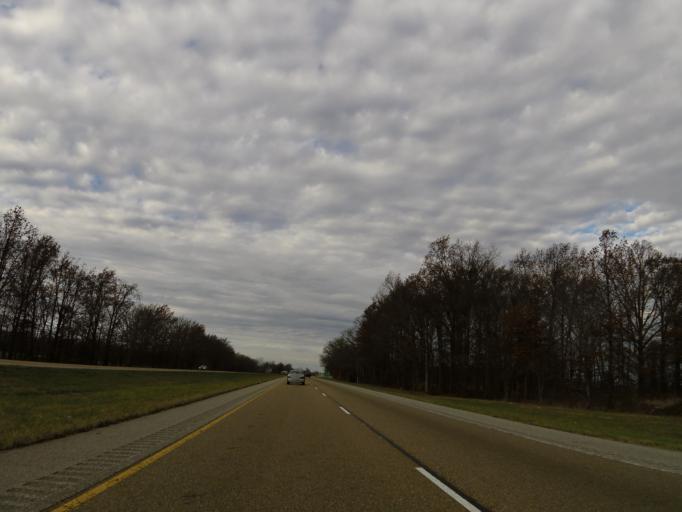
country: US
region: Illinois
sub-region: Clinton County
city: Wamac
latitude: 38.3877
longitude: -89.1525
